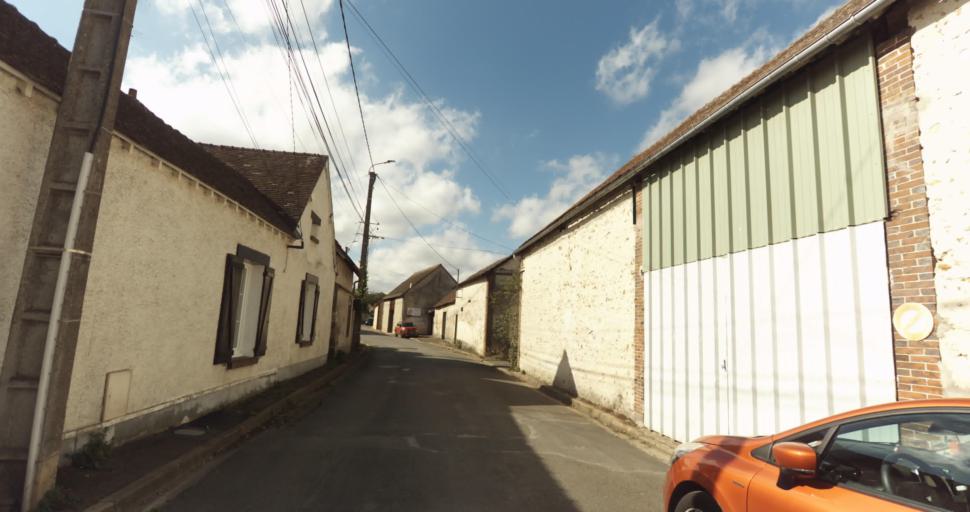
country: FR
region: Centre
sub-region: Departement d'Eure-et-Loir
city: Garnay
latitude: 48.7271
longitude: 1.3270
